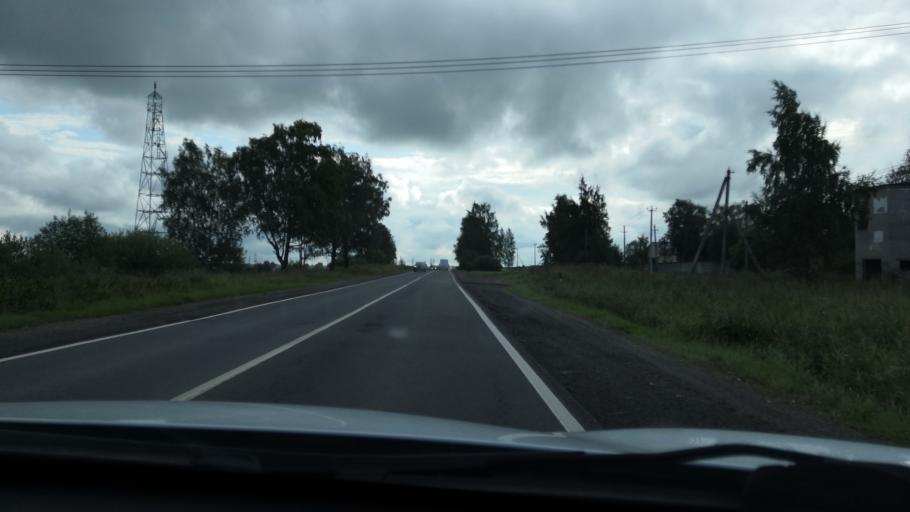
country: RU
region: St.-Petersburg
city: Tyarlevo
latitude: 59.7094
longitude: 30.4968
